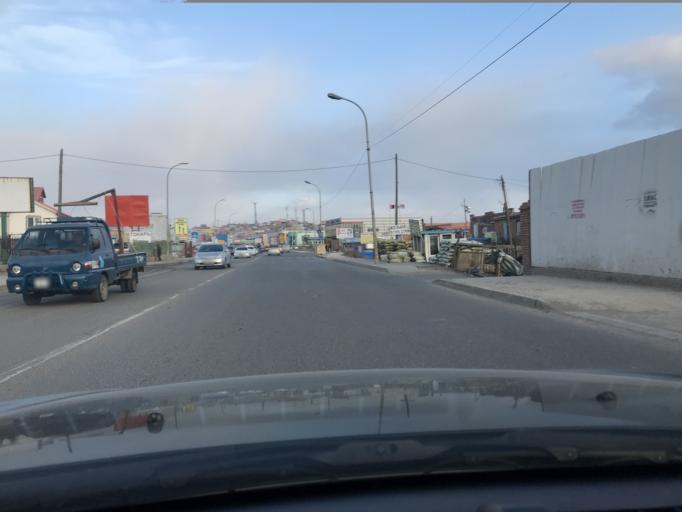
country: MN
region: Ulaanbaatar
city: Ulaanbaatar
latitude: 47.9242
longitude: 106.9901
